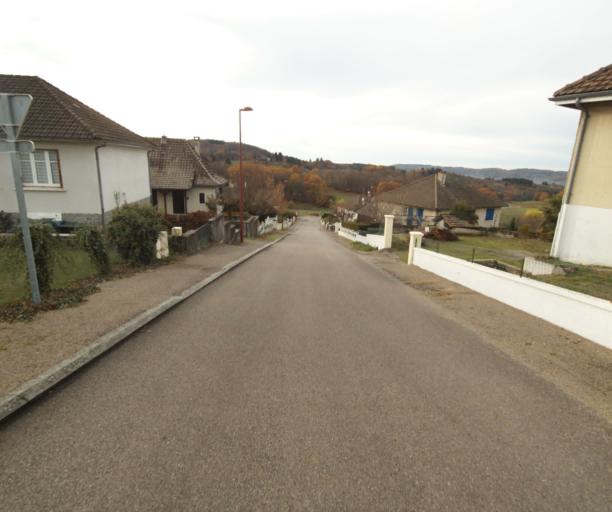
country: FR
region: Limousin
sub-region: Departement de la Correze
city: Sainte-Fortunade
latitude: 45.2124
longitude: 1.7693
